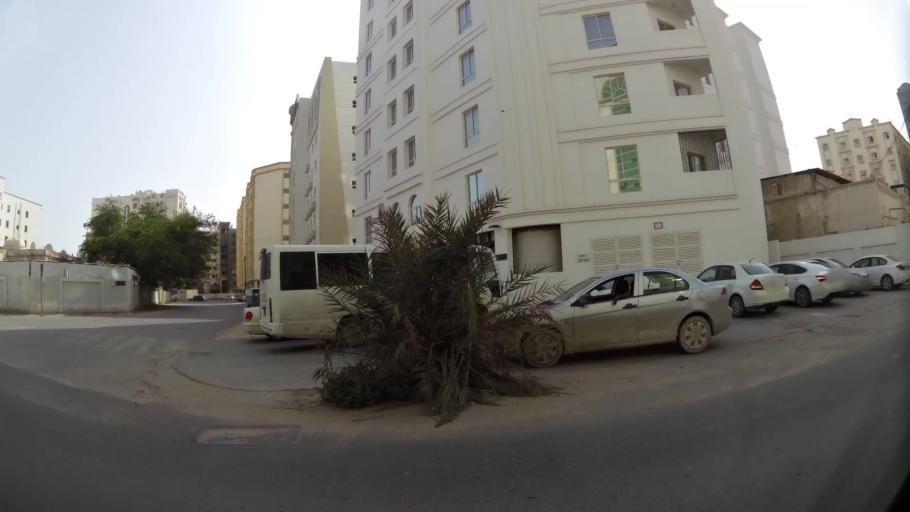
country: QA
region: Baladiyat ad Dawhah
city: Doha
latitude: 25.2825
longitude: 51.5101
